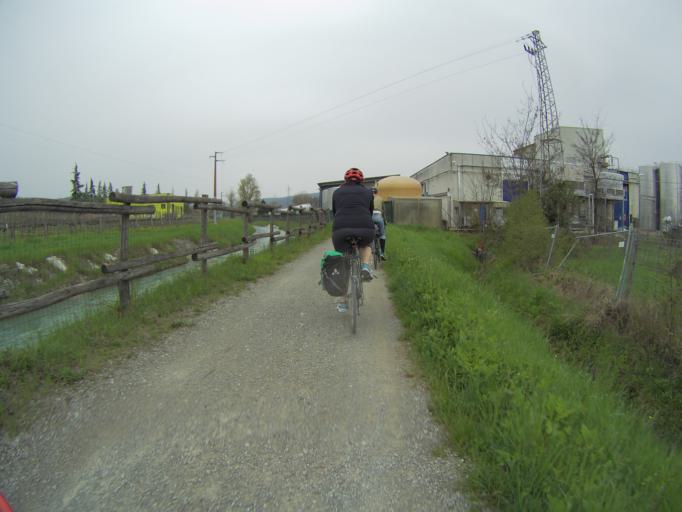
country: IT
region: Emilia-Romagna
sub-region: Provincia di Reggio Emilia
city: Ciano d'Enza
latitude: 44.6097
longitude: 10.4086
